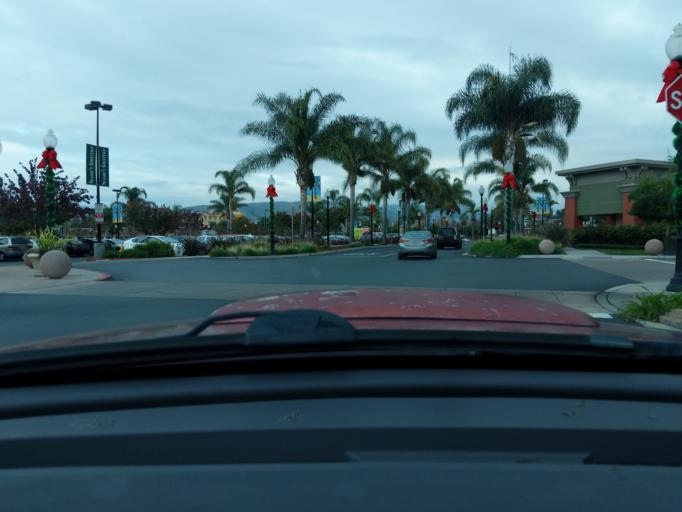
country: US
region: California
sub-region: Santa Clara County
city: Milpitas
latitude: 37.4343
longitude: -121.8984
